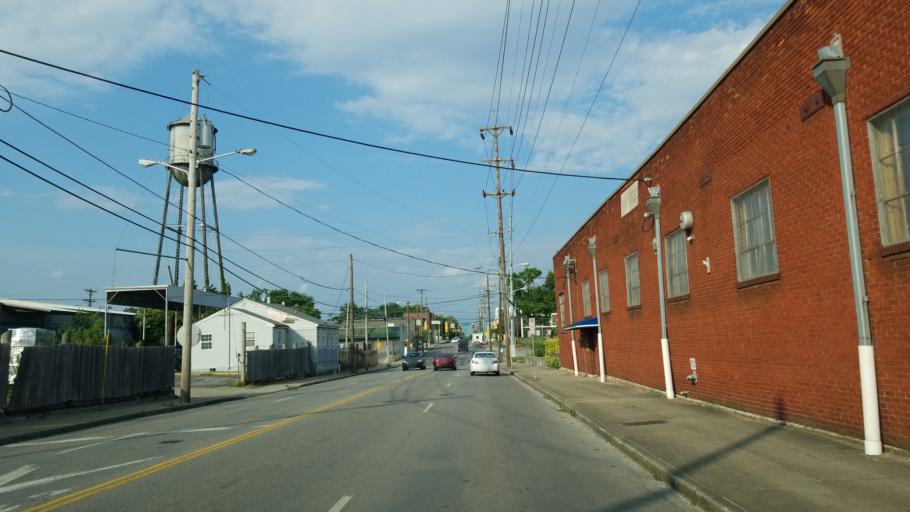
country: US
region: Tennessee
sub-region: Davidson County
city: Nashville
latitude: 36.1445
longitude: -86.7677
